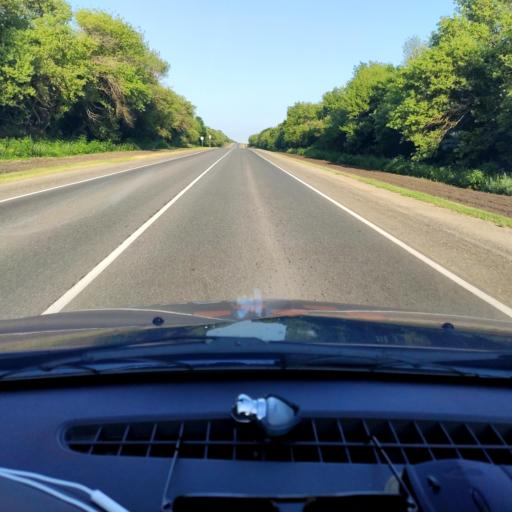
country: RU
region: Orjol
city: Livny
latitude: 52.4267
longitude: 37.7649
